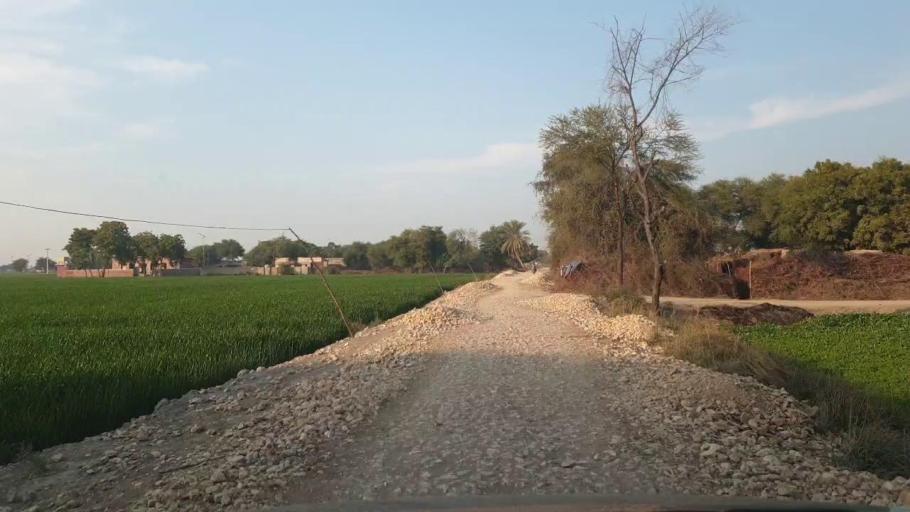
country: PK
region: Sindh
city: Shahpur Chakar
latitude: 26.1529
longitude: 68.6172
